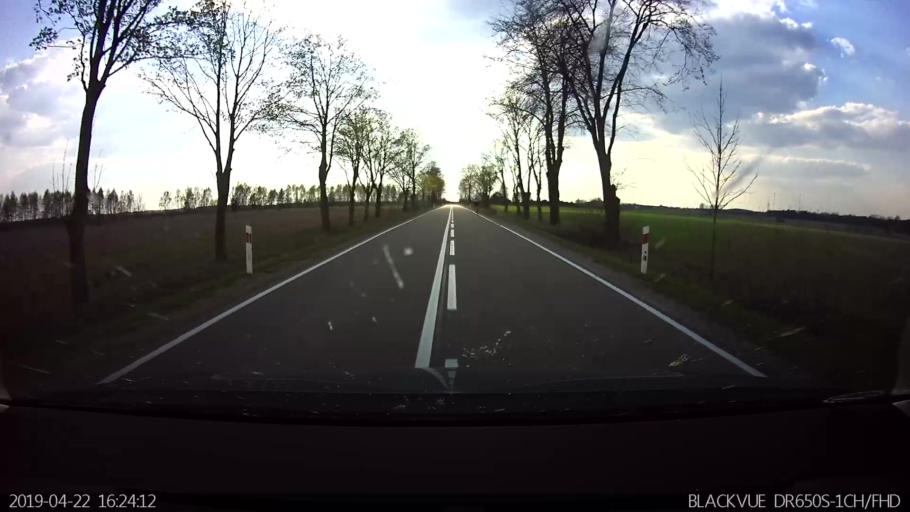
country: PL
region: Podlasie
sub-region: Powiat hajnowski
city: Kleszczele
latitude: 52.5558
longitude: 23.2695
